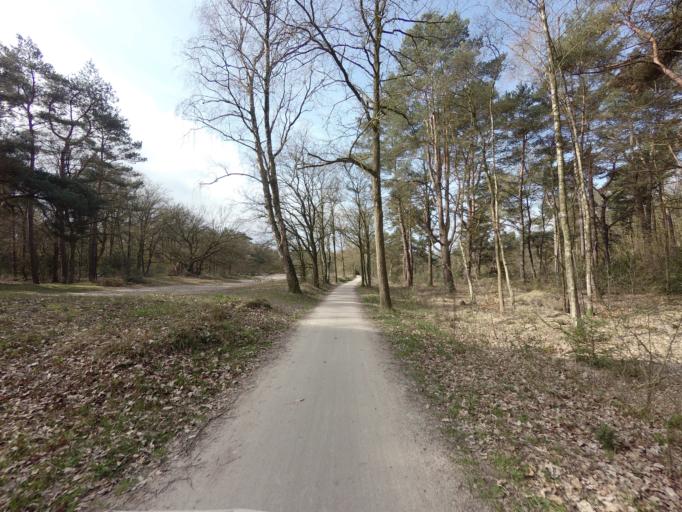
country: NL
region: North Holland
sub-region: Gemeente Blaricum
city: Blaricum
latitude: 52.2659
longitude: 5.2397
